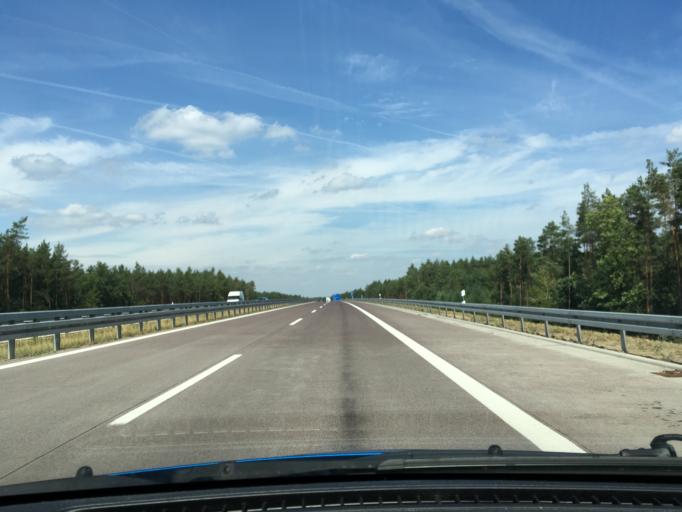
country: DE
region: Mecklenburg-Vorpommern
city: Gross Laasch
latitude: 53.3343
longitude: 11.5248
